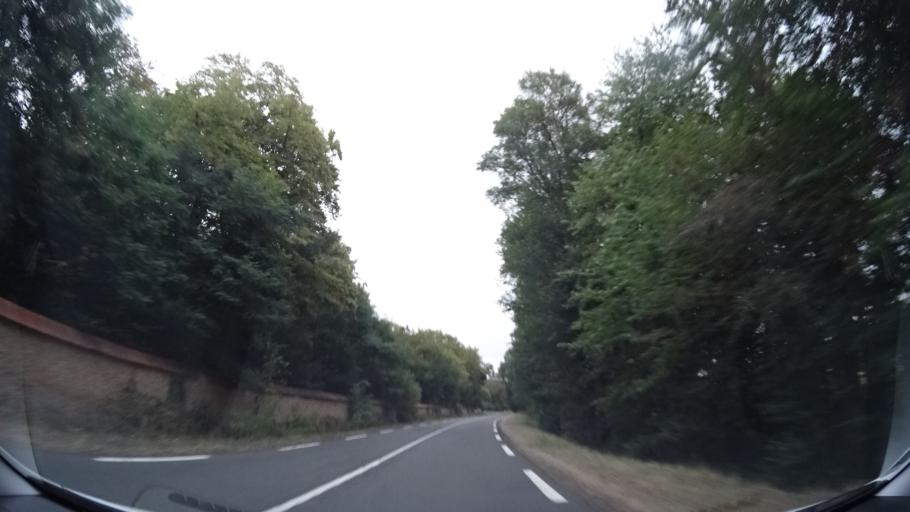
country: FR
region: Centre
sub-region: Departement du Loiret
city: Douchy
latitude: 47.9467
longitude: 3.0256
